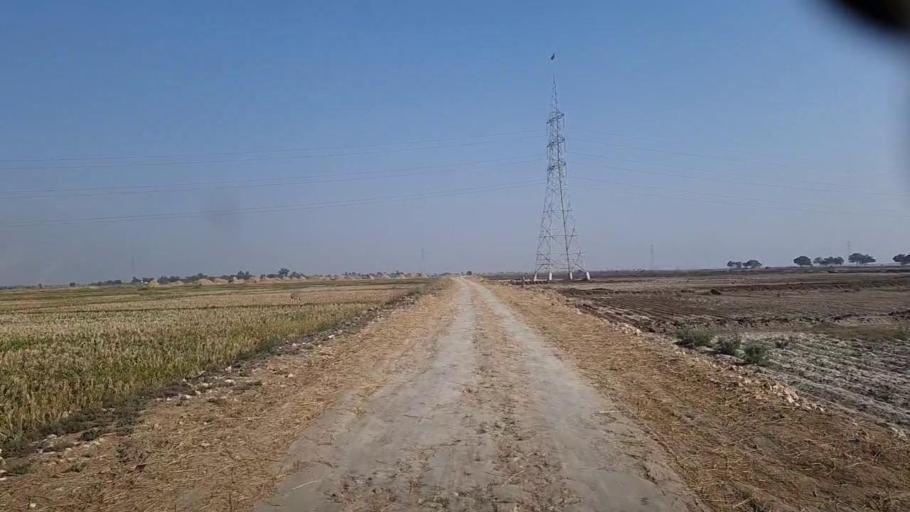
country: PK
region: Sindh
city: Jacobabad
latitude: 28.3074
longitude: 68.5945
